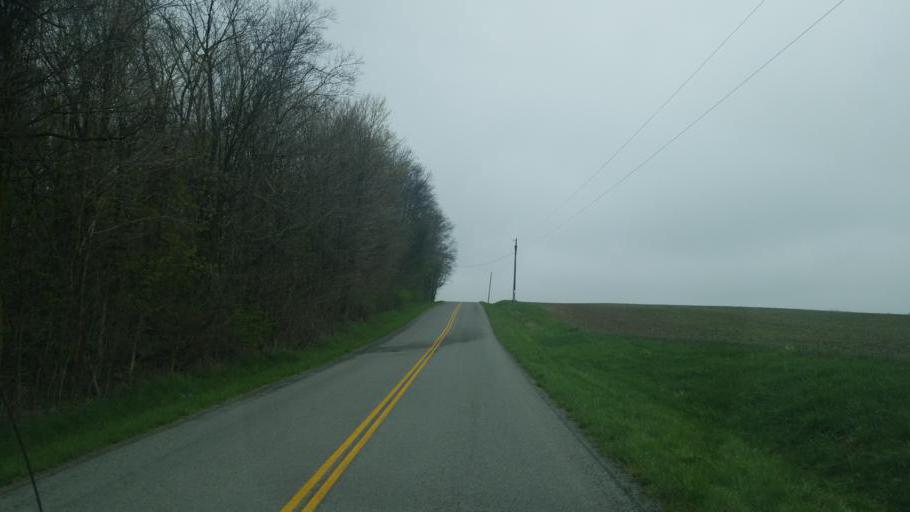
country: US
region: Ohio
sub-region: Logan County
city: Northwood
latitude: 40.4994
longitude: -83.6764
